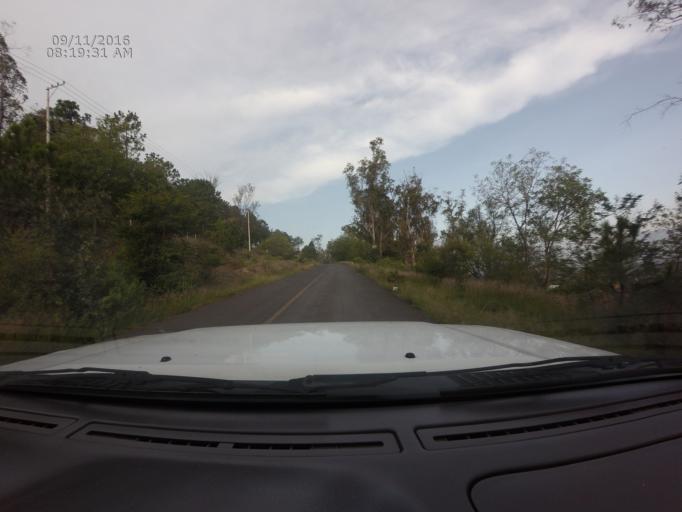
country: MX
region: Michoacan
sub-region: Morelia
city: Morelos
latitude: 19.6361
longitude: -101.2365
